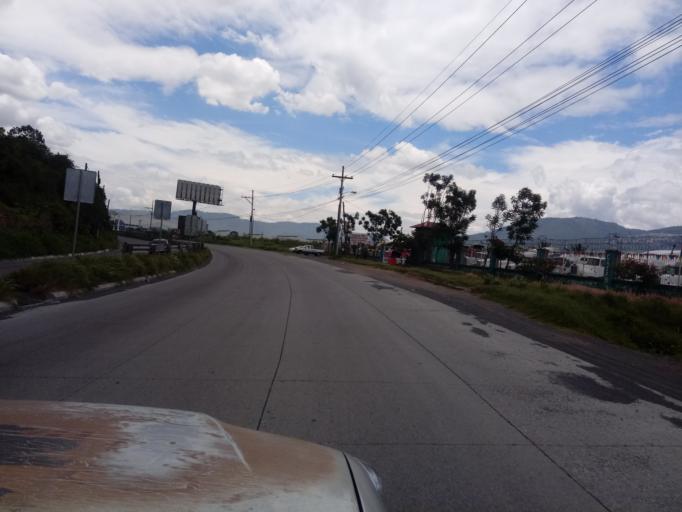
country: GT
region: Escuintla
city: San Vicente Pacaya
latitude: 14.4481
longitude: -90.6446
